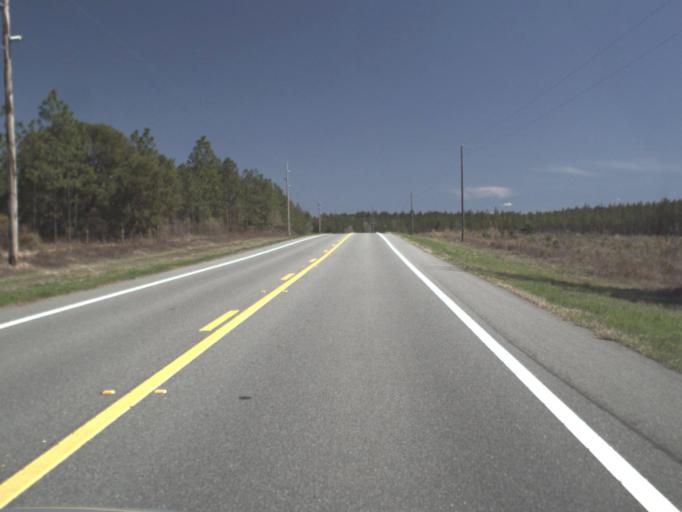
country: US
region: Florida
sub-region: Gadsden County
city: Quincy
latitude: 30.4163
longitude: -84.6566
